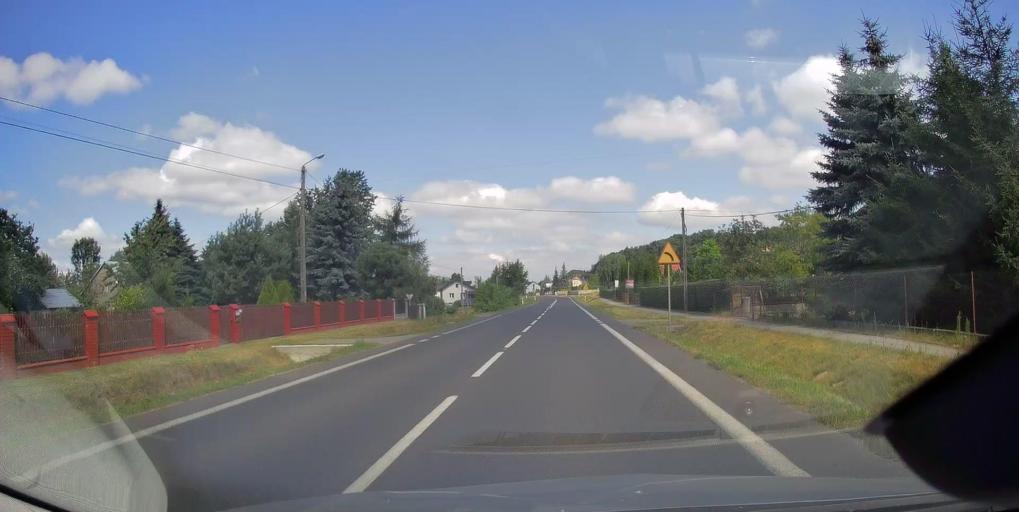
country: PL
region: Subcarpathian Voivodeship
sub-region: Powiat debicki
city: Brzeznica
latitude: 50.1151
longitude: 21.4898
